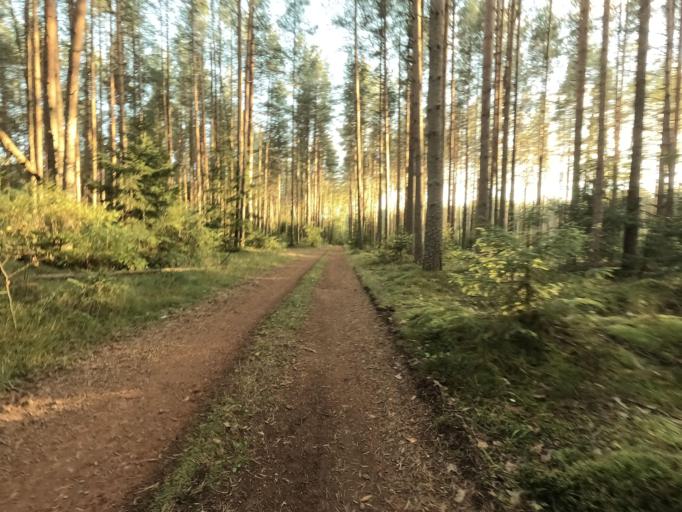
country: RU
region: Leningrad
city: Otradnoye
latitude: 59.8384
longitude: 30.7719
